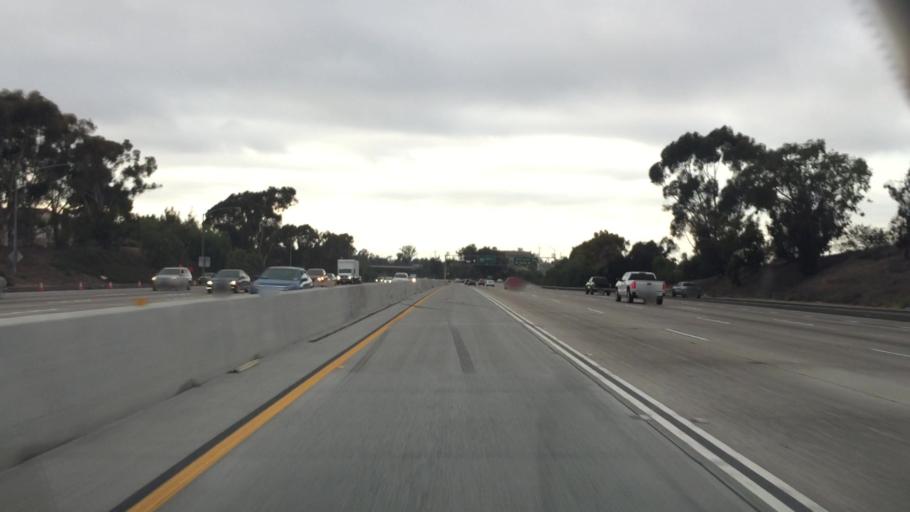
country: US
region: California
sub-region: San Diego County
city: National City
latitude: 32.6790
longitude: -117.0855
